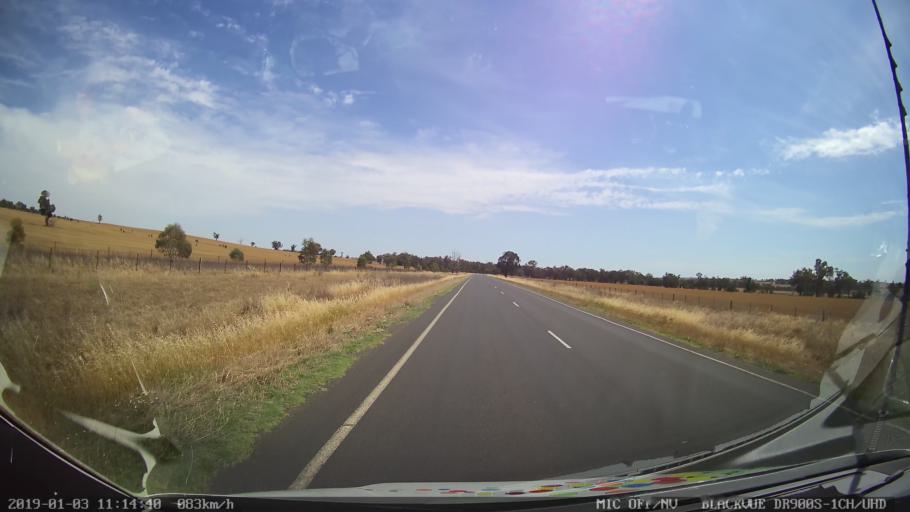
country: AU
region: New South Wales
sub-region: Young
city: Young
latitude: -34.1732
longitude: 148.2612
